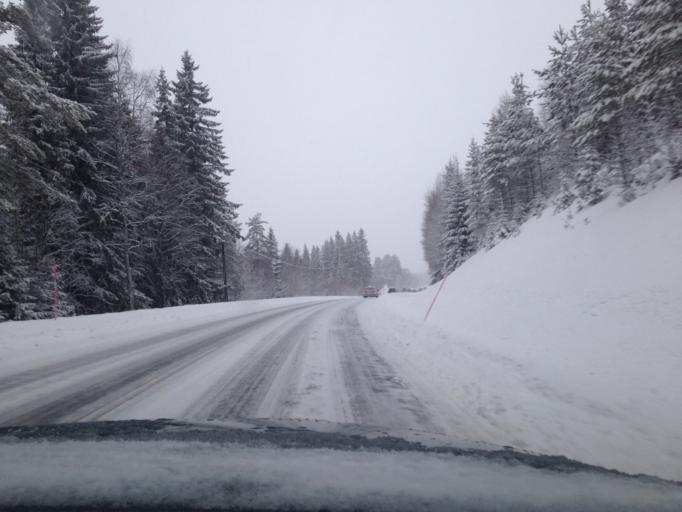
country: SE
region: Dalarna
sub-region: Malung-Saelens kommun
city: Malung
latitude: 61.0266
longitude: 13.3386
